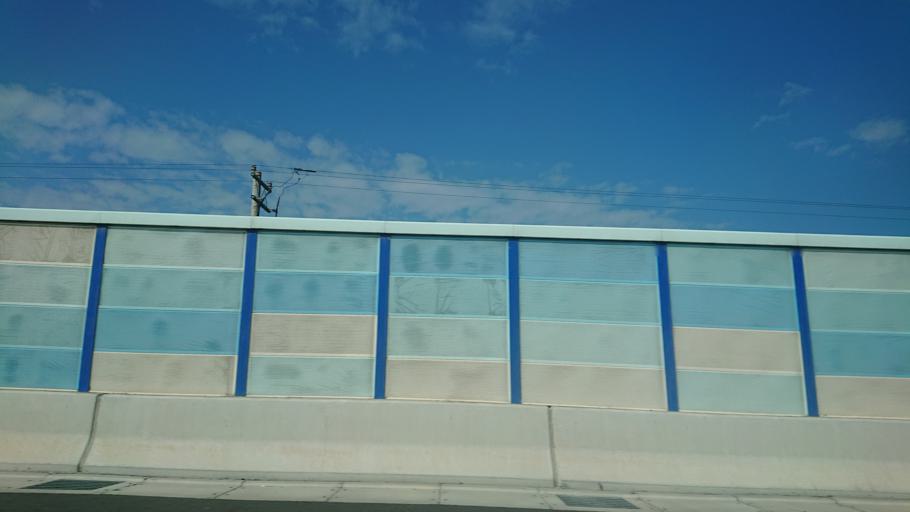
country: TW
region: Taiwan
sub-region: Changhua
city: Chang-hua
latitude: 23.9545
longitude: 120.3313
